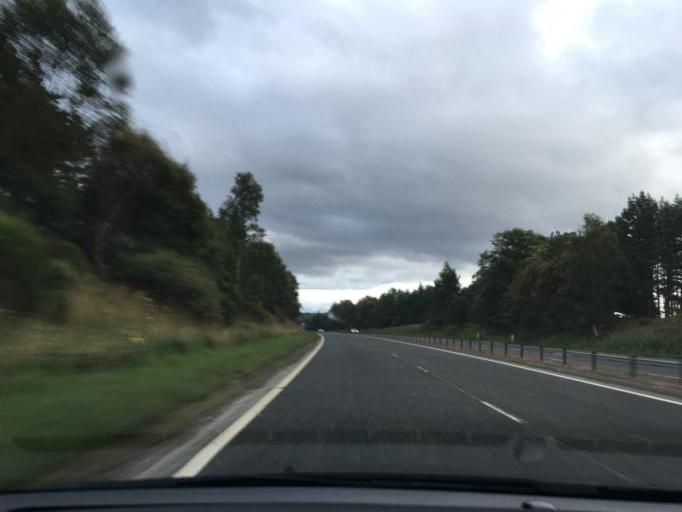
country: GB
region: Scotland
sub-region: Highland
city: Inverness
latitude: 57.4374
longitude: -4.1399
